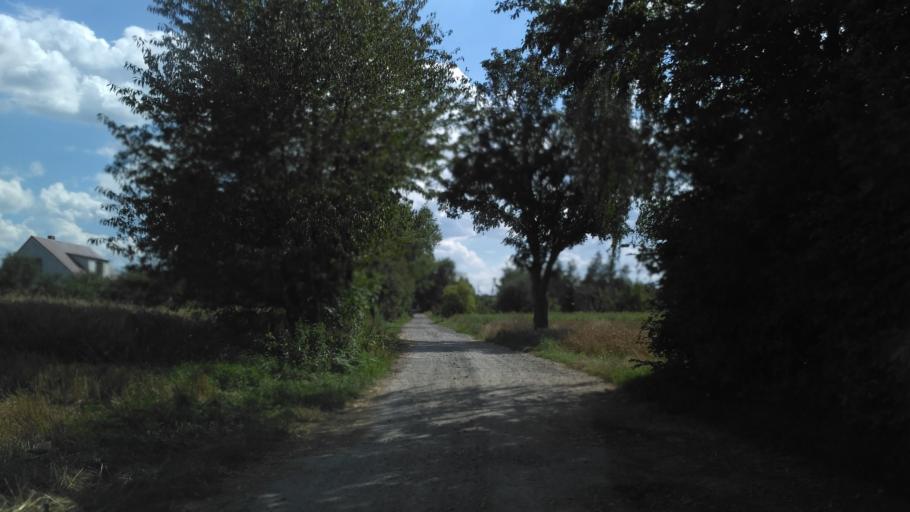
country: PL
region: Lublin Voivodeship
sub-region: Powiat leczynski
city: Milejow
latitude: 51.2057
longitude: 22.8697
